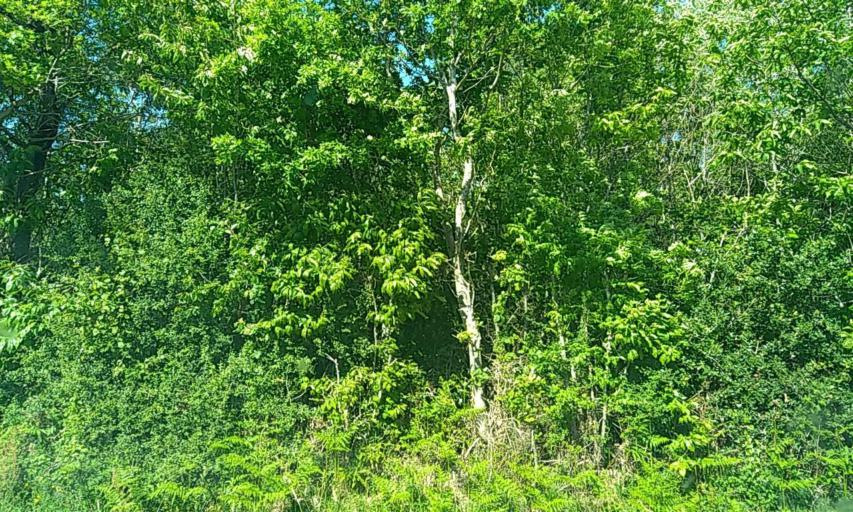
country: FR
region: Poitou-Charentes
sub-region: Departement des Deux-Sevres
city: Boisme
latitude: 46.7984
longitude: -0.4539
